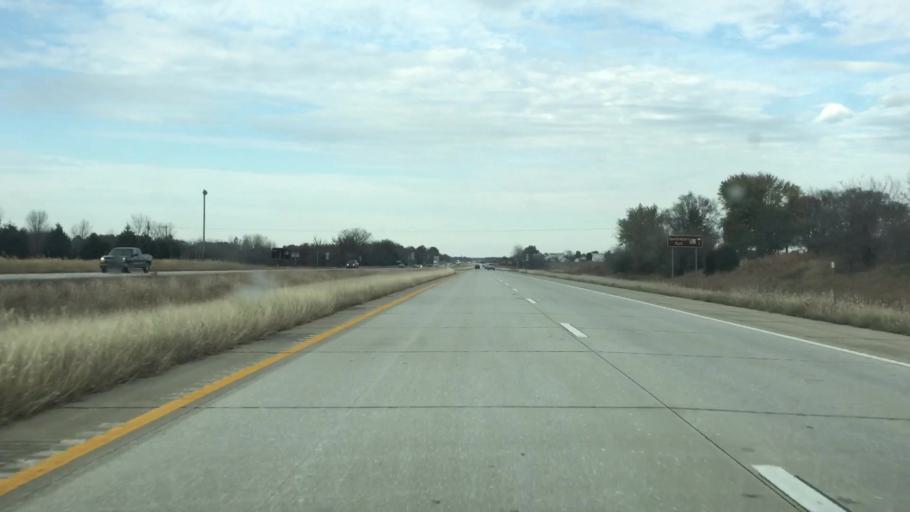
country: US
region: Missouri
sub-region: Henry County
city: Clinton
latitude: 38.2990
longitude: -93.7587
